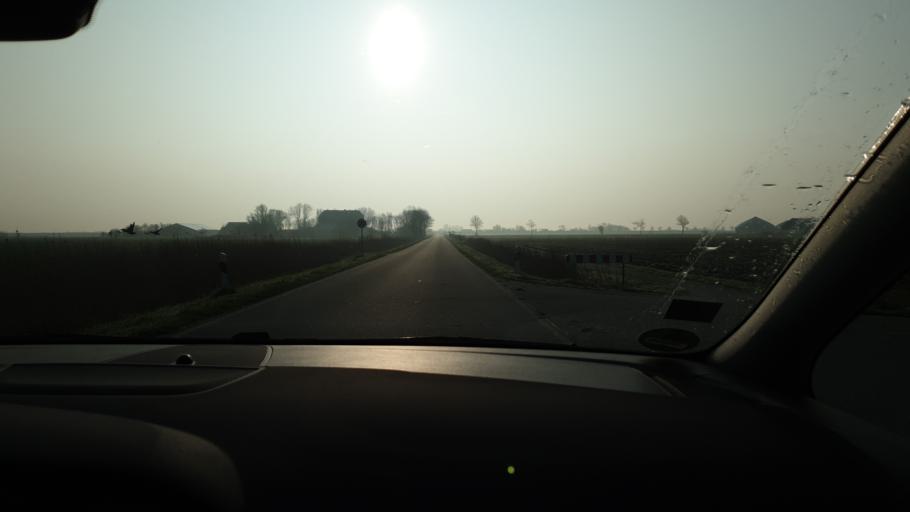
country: DE
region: Schleswig-Holstein
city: Elisabeth-Sophien-Koog
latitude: 54.4984
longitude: 8.8991
